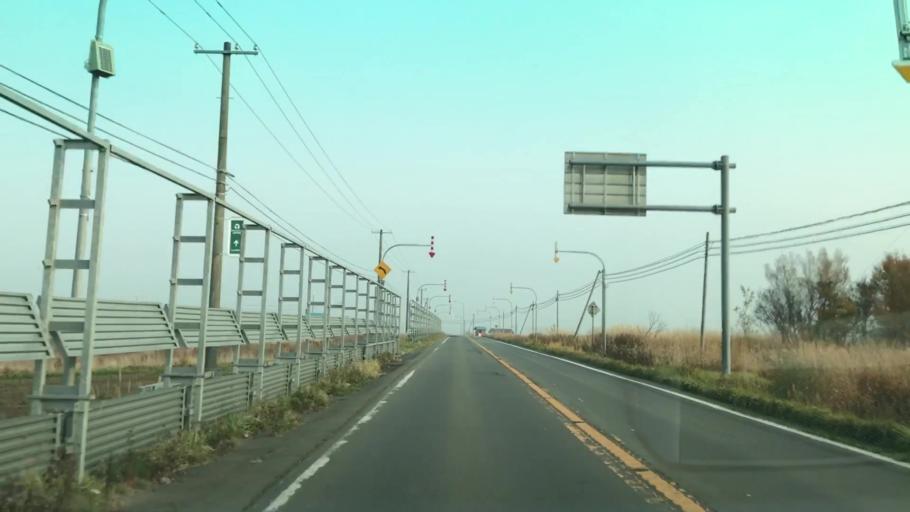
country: JP
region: Hokkaido
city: Ishikari
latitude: 43.2783
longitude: 141.4088
